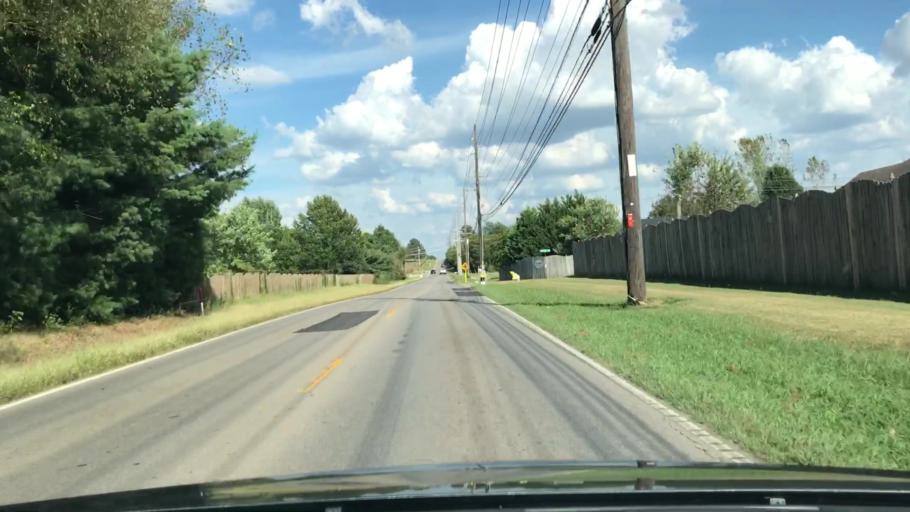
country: US
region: Alabama
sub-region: Madison County
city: Harvest
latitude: 34.8085
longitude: -86.7430
